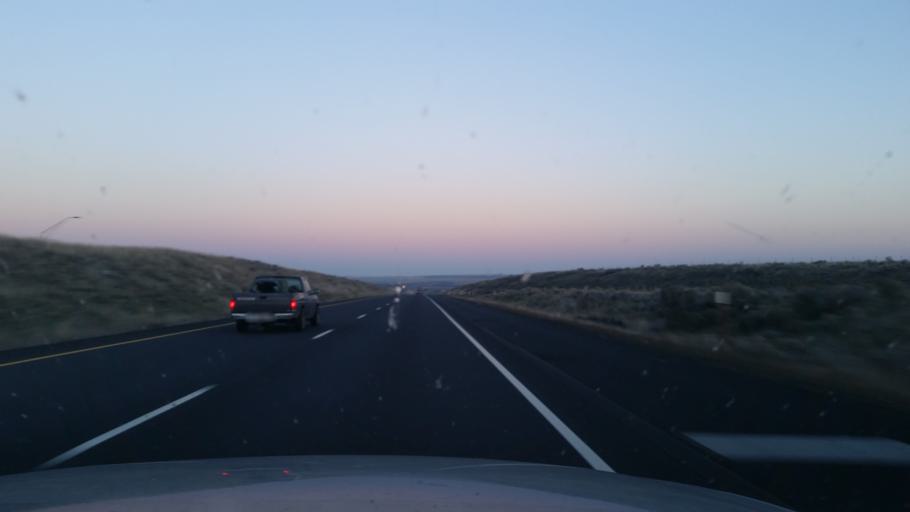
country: US
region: Washington
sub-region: Adams County
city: Ritzville
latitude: 47.0968
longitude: -118.6651
